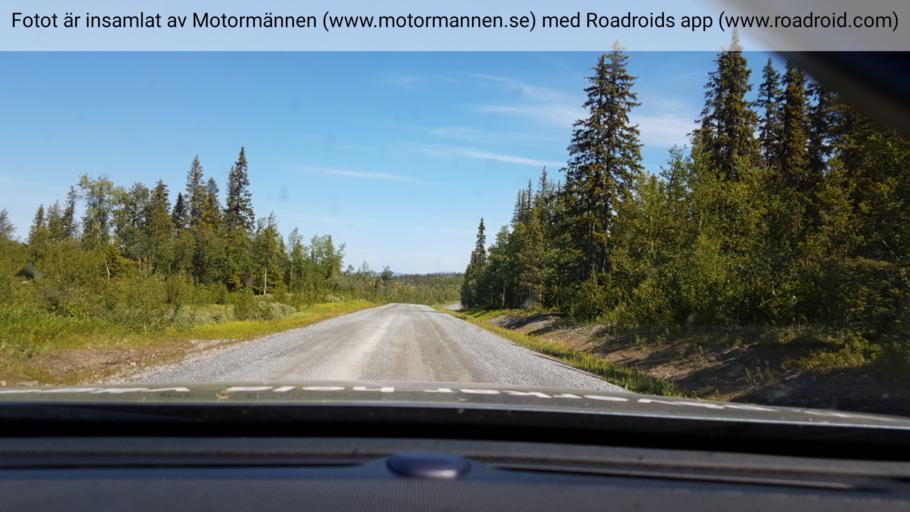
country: SE
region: Vaesterbotten
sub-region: Vilhelmina Kommun
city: Sjoberg
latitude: 64.7679
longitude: 15.9036
